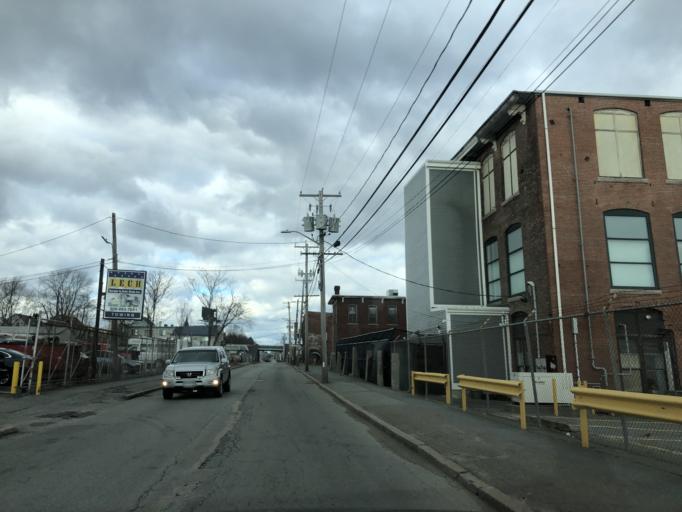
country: US
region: Massachusetts
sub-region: Bristol County
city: New Bedford
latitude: 41.6521
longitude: -70.9245
